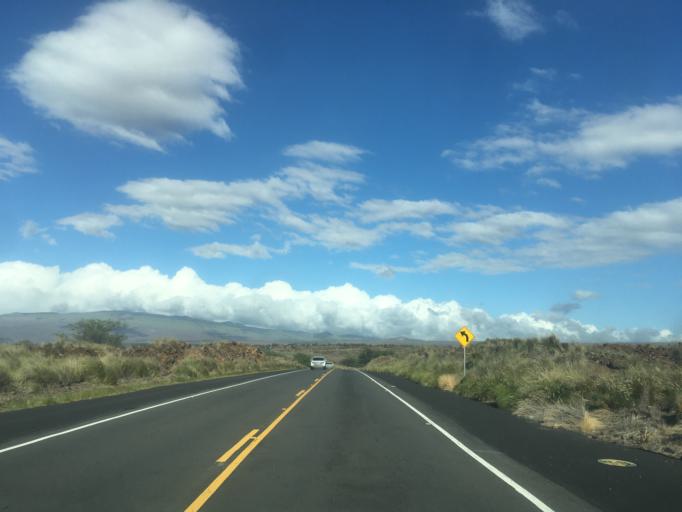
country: US
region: Hawaii
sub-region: Hawaii County
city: Waikoloa Village
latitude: 19.9142
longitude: -155.8089
